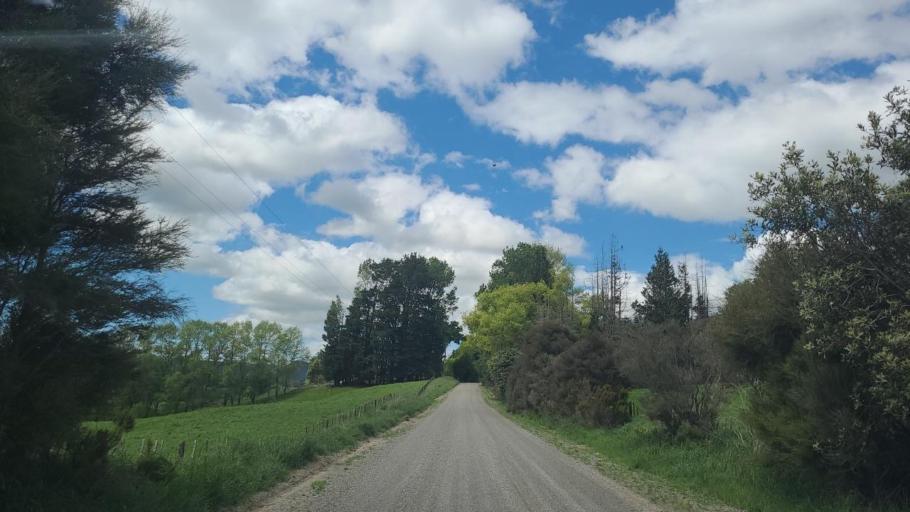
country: NZ
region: Hawke's Bay
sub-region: Napier City
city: Napier
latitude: -39.2214
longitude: 176.7602
